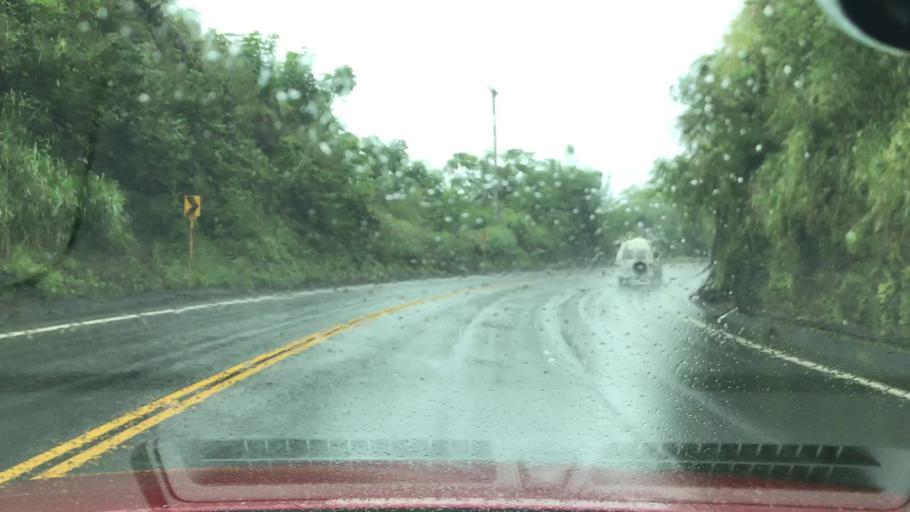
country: US
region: Hawaii
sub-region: Hawaii County
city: Pepeekeo
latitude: 19.9883
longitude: -155.2450
